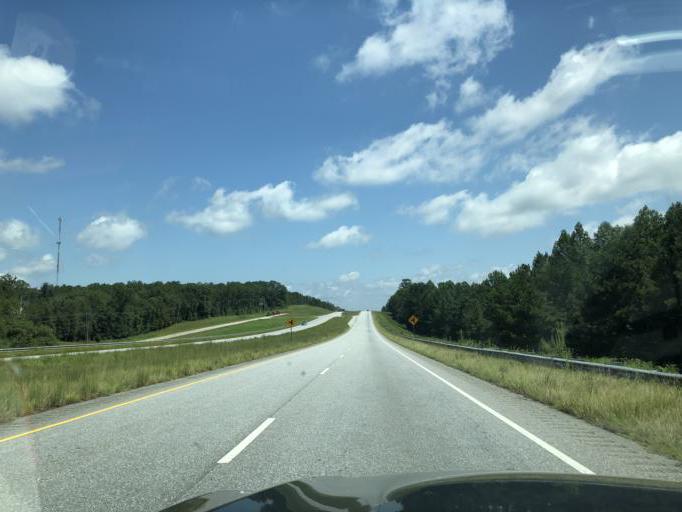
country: US
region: Alabama
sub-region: Barbour County
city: Eufaula
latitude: 31.7628
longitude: -85.2009
